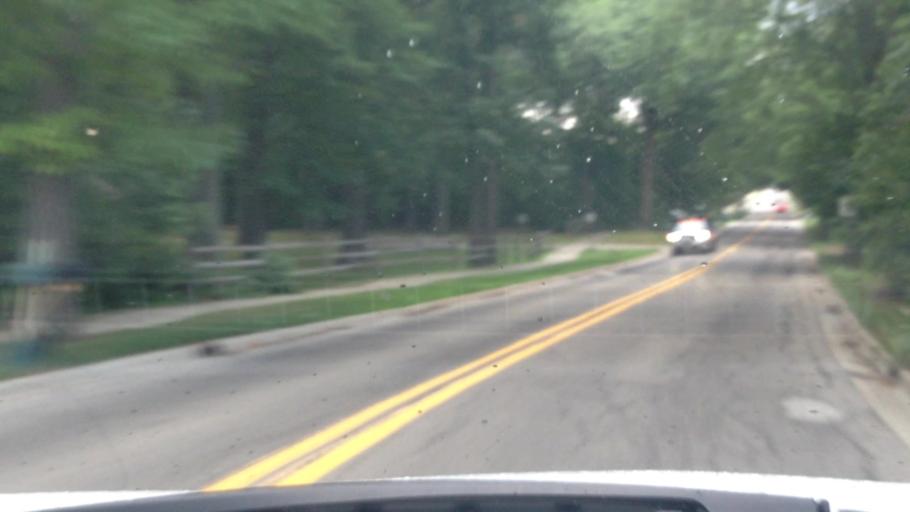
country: US
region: Michigan
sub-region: Oakland County
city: Clarkston
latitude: 42.7525
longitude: -83.3509
